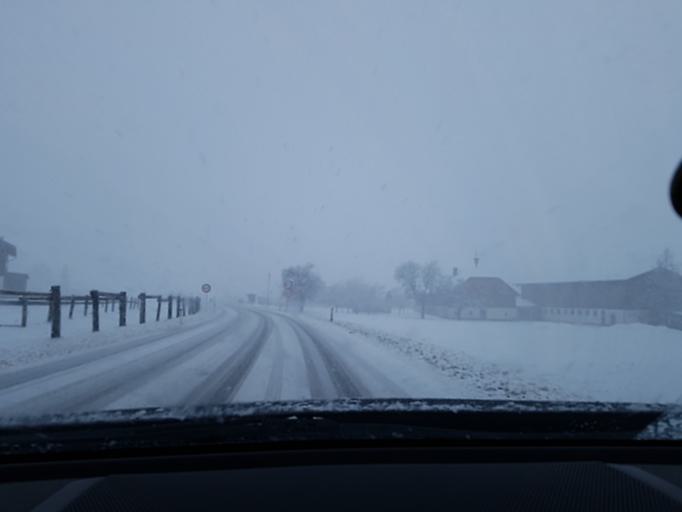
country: AT
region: Salzburg
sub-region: Politischer Bezirk Hallein
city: Abtenau
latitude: 47.5616
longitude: 13.3745
